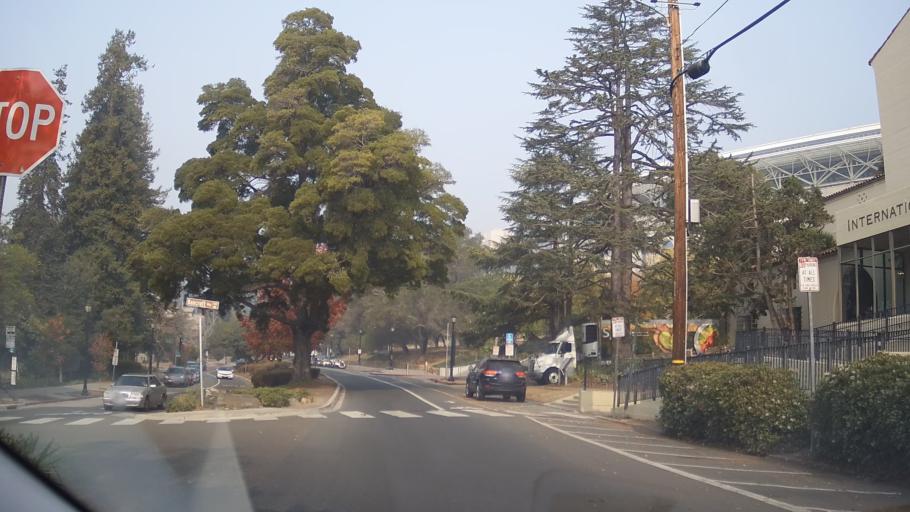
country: US
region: California
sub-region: Alameda County
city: Berkeley
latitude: 37.8694
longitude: -122.2522
